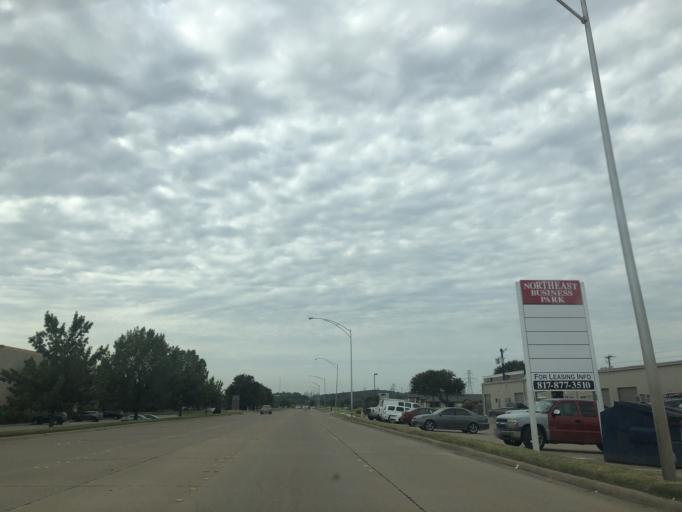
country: US
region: Texas
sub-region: Tarrant County
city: Richland Hills
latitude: 32.7904
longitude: -97.2212
